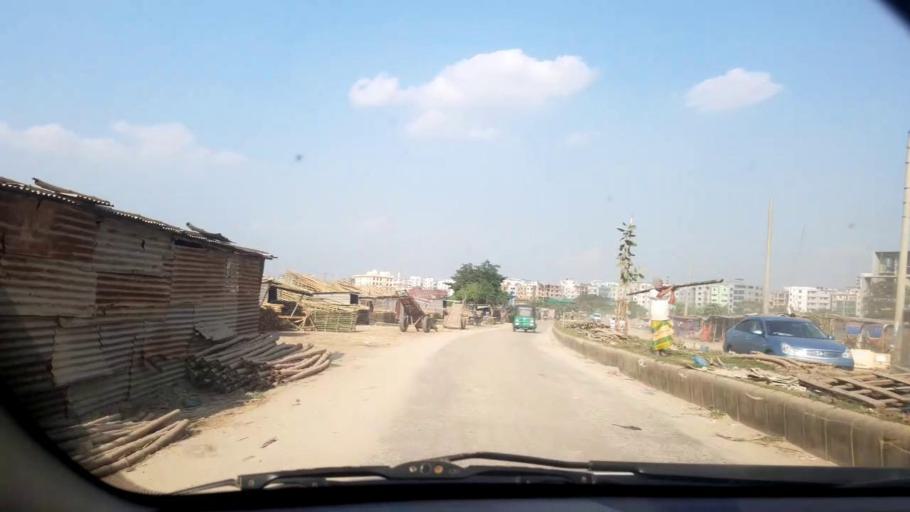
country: BD
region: Dhaka
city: Tungi
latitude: 23.8688
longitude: 90.3765
